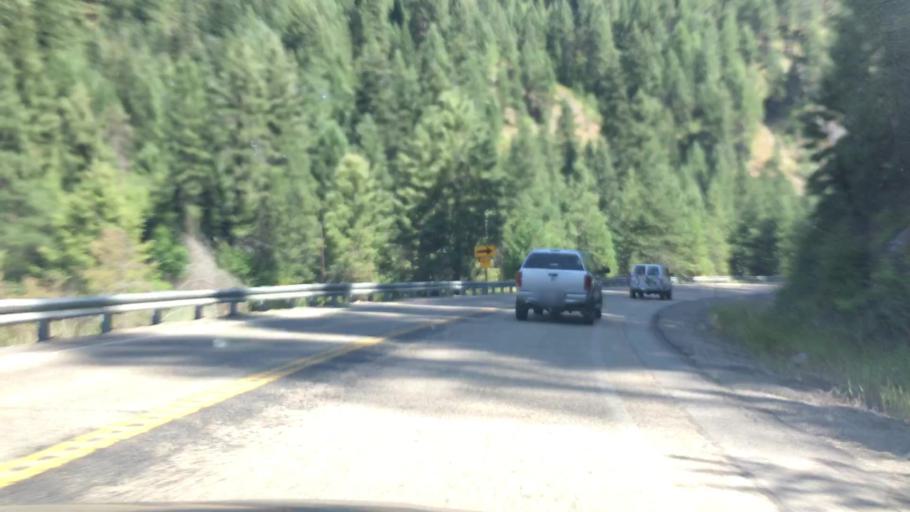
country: US
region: Idaho
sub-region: Valley County
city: Cascade
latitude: 44.1505
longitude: -116.1130
